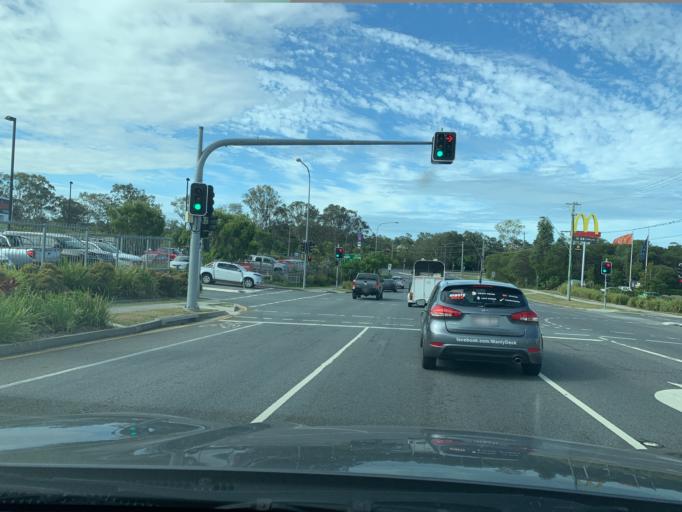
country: AU
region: Queensland
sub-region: Brisbane
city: Wynnum West
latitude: -27.4777
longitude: 153.1404
